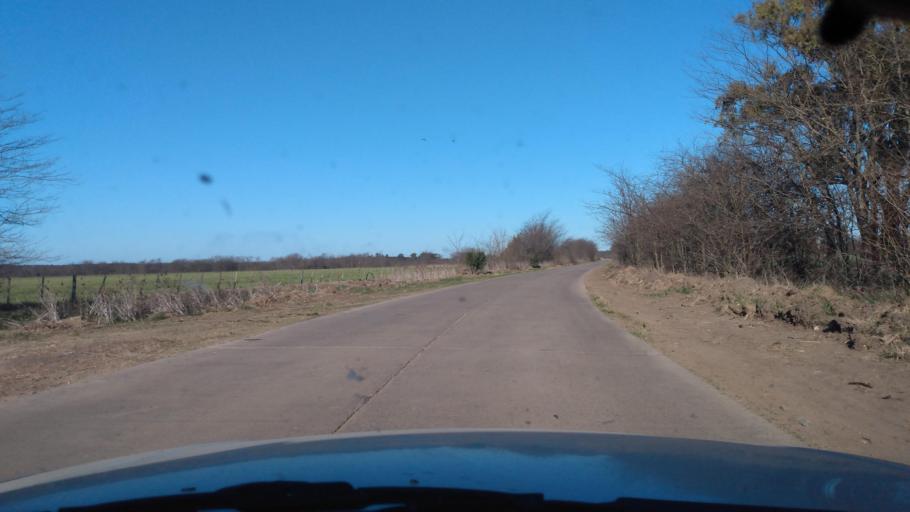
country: AR
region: Buenos Aires
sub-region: Partido de Lujan
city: Lujan
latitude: -34.6147
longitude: -59.2659
